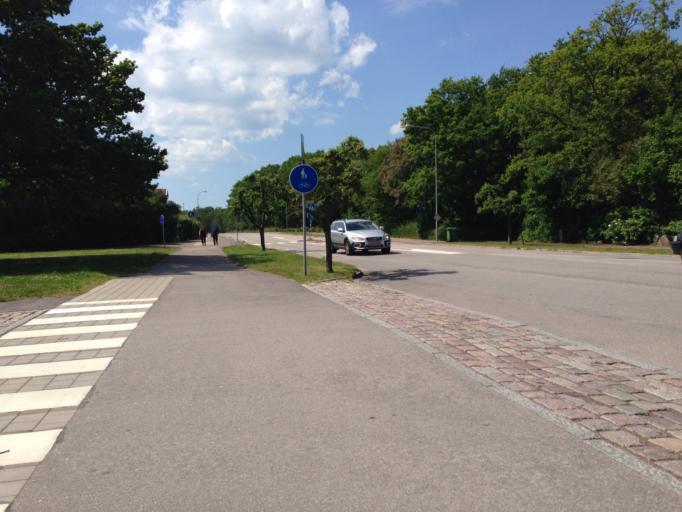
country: SE
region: Kalmar
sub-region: Kalmar Kommun
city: Kalmar
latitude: 56.6551
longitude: 16.3339
